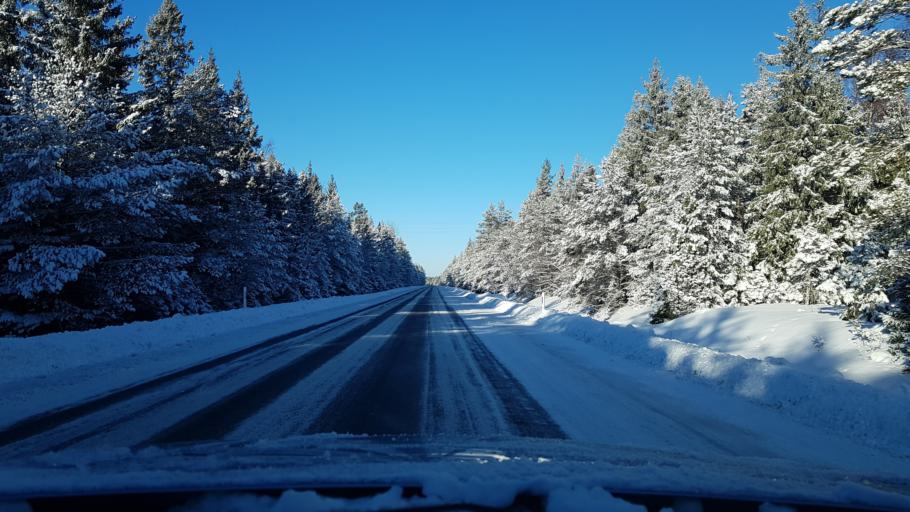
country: EE
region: Hiiumaa
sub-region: Kaerdla linn
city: Kardla
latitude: 58.9833
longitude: 22.8039
